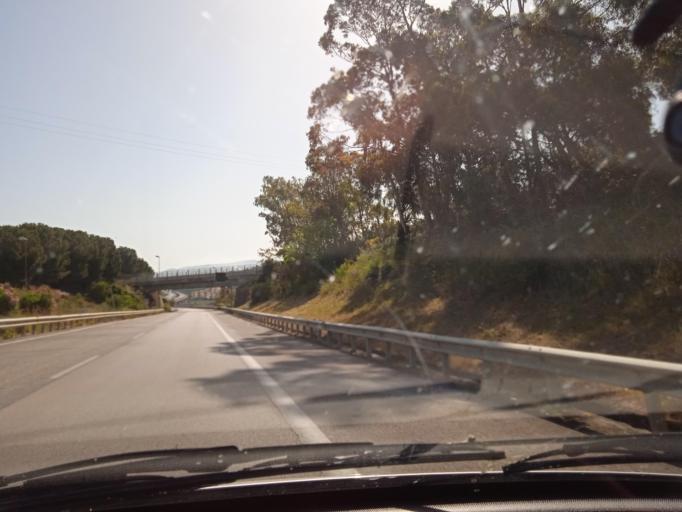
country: IT
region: Sicily
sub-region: Messina
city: Acquedolci
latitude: 38.0450
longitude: 14.5520
